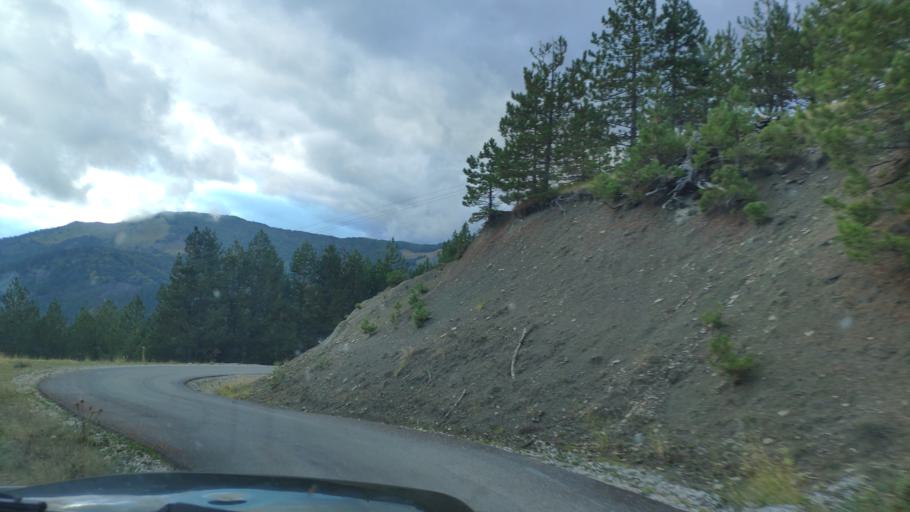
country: AL
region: Korce
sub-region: Rrethi i Kolonjes
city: Erseke
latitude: 40.2924
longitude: 20.8652
